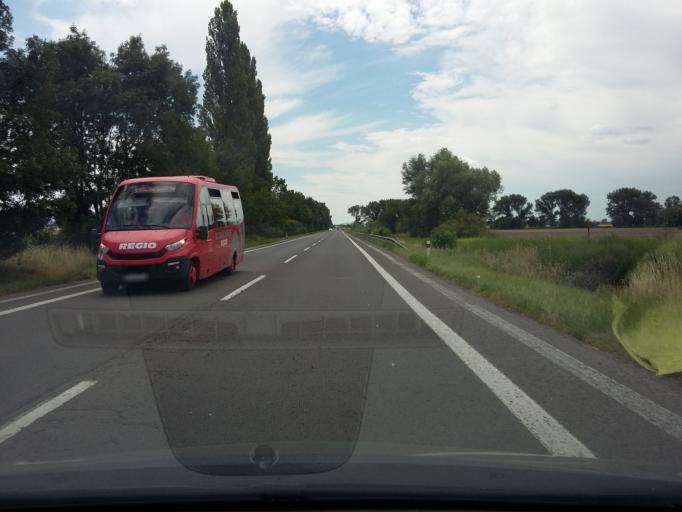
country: SK
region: Bratislavsky
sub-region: Okres Malacky
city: Malacky
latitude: 48.4611
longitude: 17.0107
